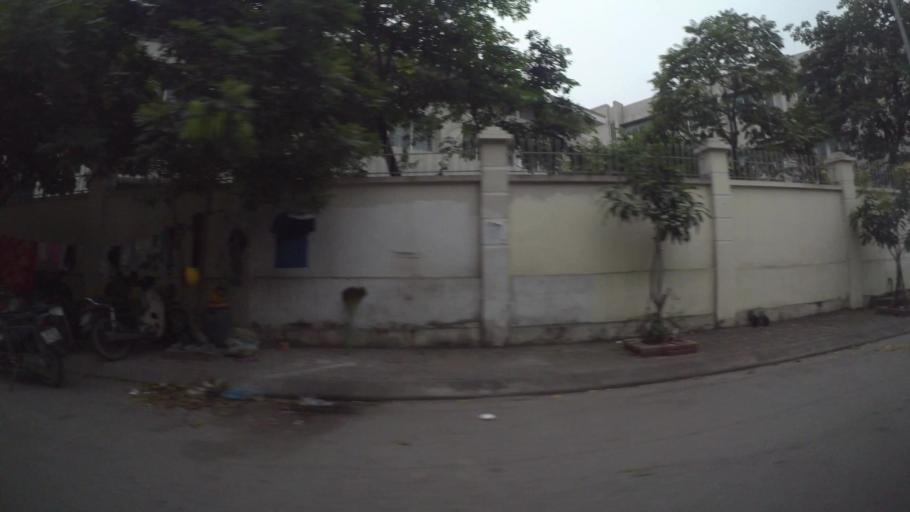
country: VN
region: Ha Noi
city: Trau Quy
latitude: 21.0413
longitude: 105.9027
